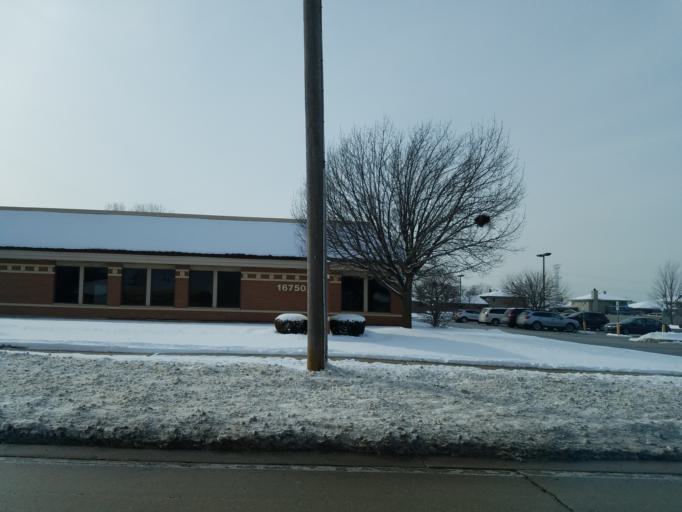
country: US
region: Illinois
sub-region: Cook County
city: Orland Hills
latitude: 41.5859
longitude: -87.8132
